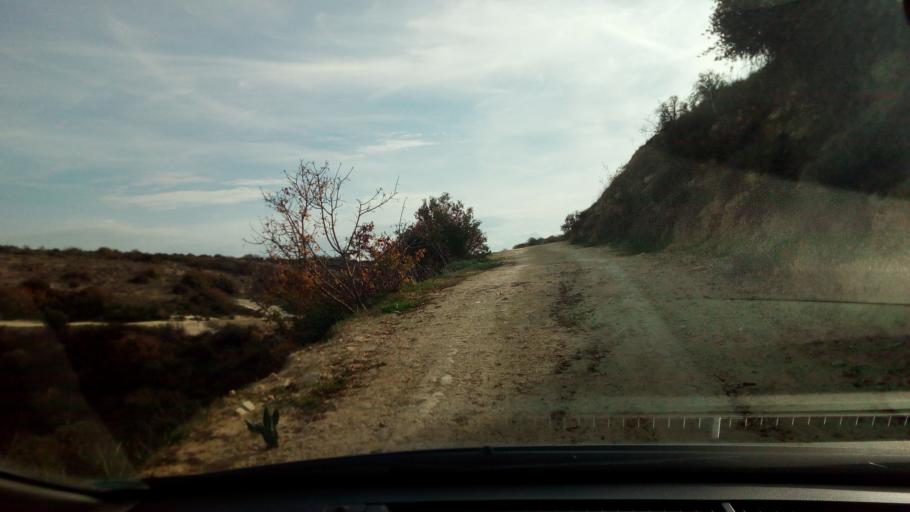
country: CY
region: Pafos
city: Mesogi
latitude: 34.7988
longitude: 32.5406
